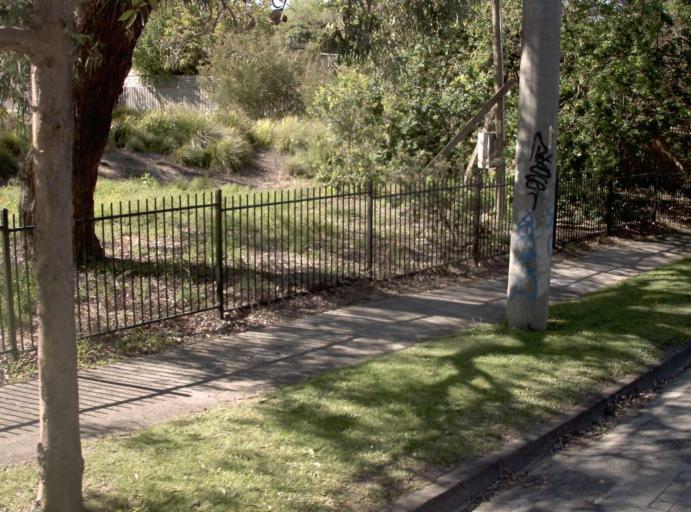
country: AU
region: Victoria
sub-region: Maroondah
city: Croydon South
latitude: -37.7978
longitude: 145.2760
